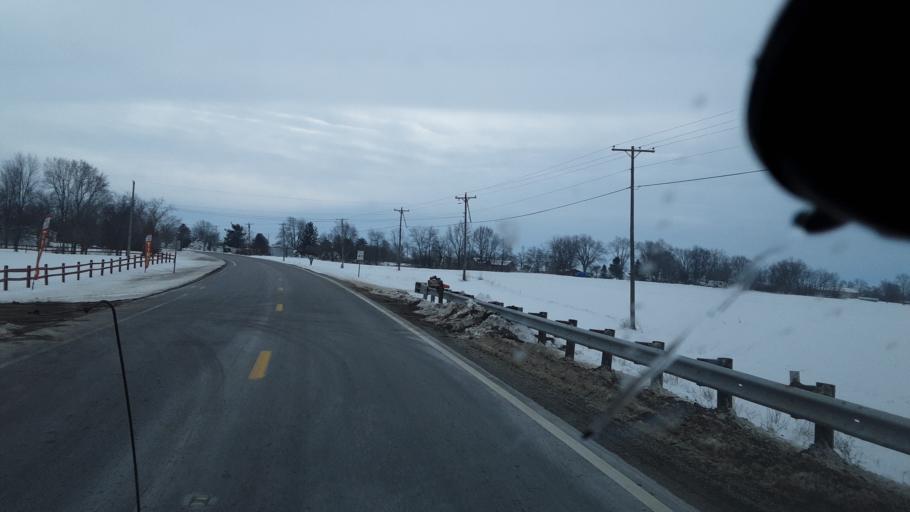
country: US
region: Ohio
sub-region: Madison County
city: London
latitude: 39.8422
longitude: -83.4673
